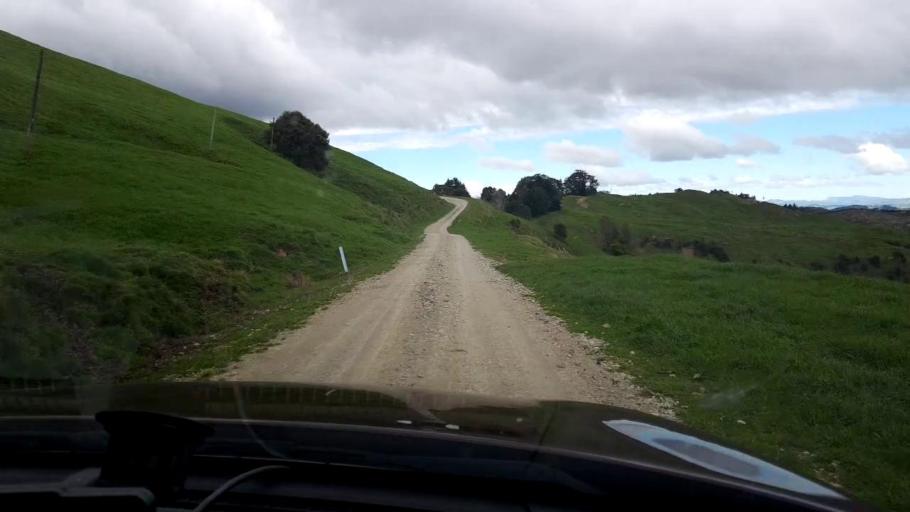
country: NZ
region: Gisborne
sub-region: Gisborne District
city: Gisborne
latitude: -38.3699
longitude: 177.9673
